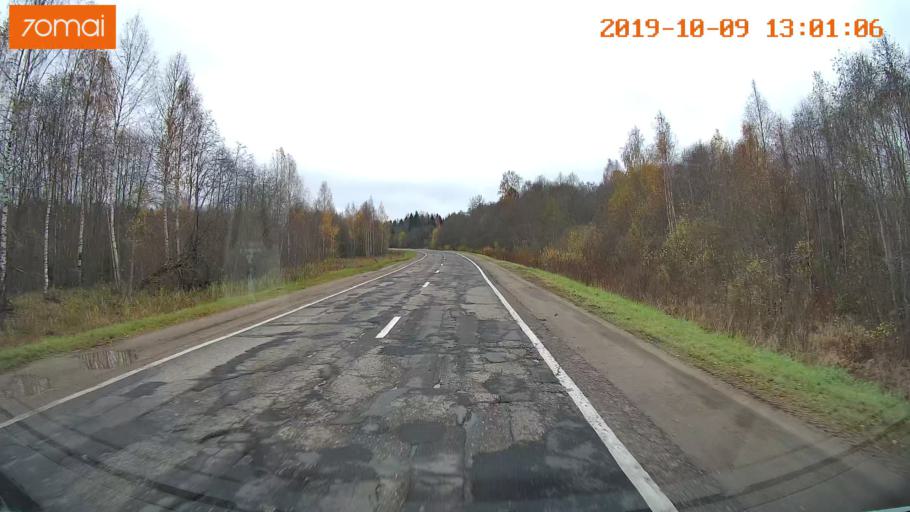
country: RU
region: Jaroslavl
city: Prechistoye
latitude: 58.3711
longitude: 40.4843
